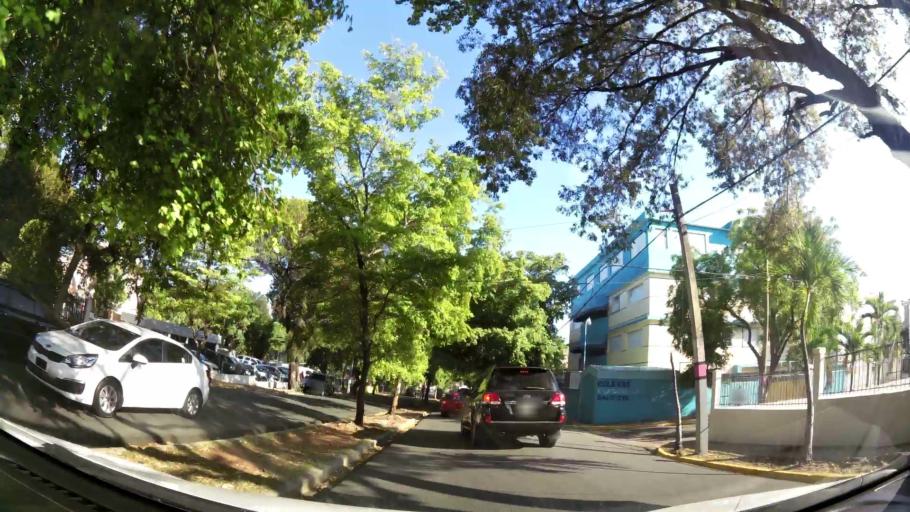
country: DO
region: Nacional
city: Bella Vista
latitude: 18.4498
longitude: -69.9361
